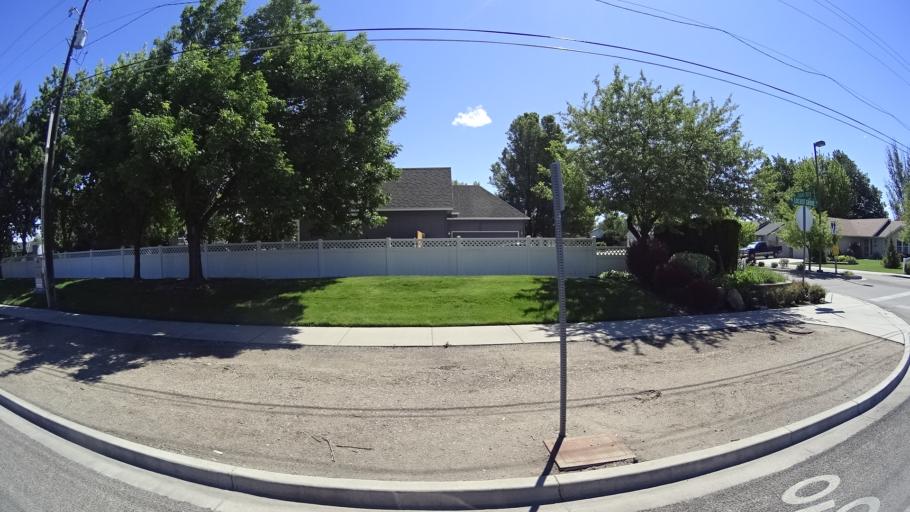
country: US
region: Idaho
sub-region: Ada County
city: Meridian
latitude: 43.6308
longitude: -116.3745
